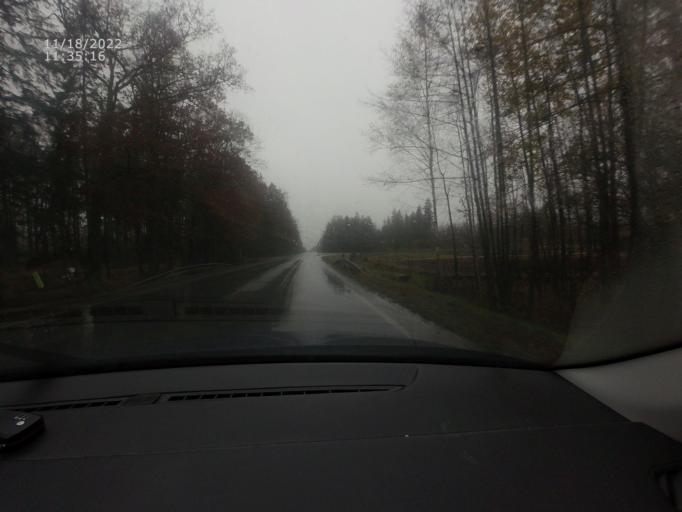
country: CZ
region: Plzensky
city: St'ahlavy
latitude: 49.7083
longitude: 13.5451
